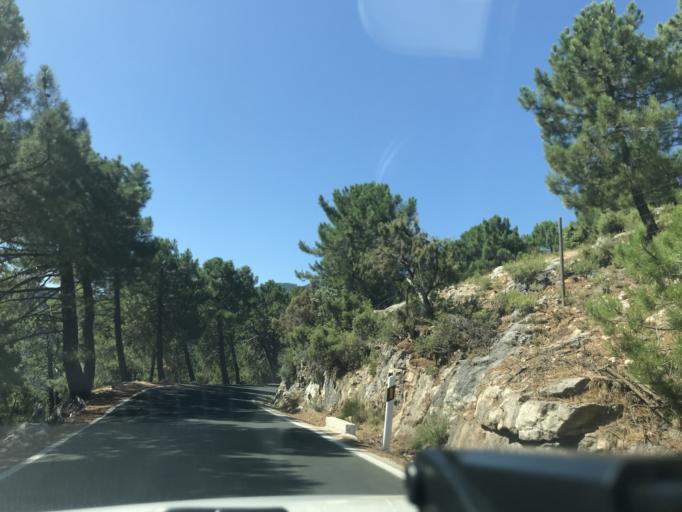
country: ES
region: Andalusia
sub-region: Provincia de Jaen
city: La Iruela
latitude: 37.9330
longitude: -2.9456
